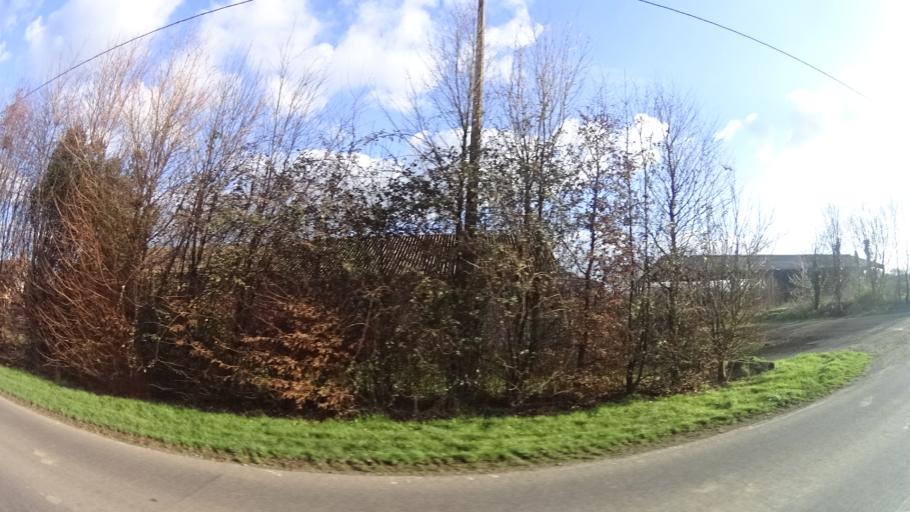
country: FR
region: Pays de la Loire
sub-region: Departement de la Loire-Atlantique
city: Guemene-Penfao
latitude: 47.5969
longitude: -1.8484
